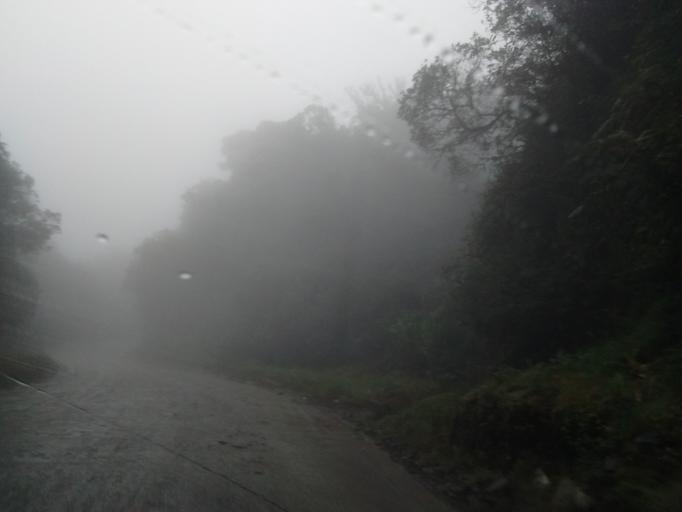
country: CO
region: Cauca
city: Paispamba
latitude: 2.1569
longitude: -76.4204
